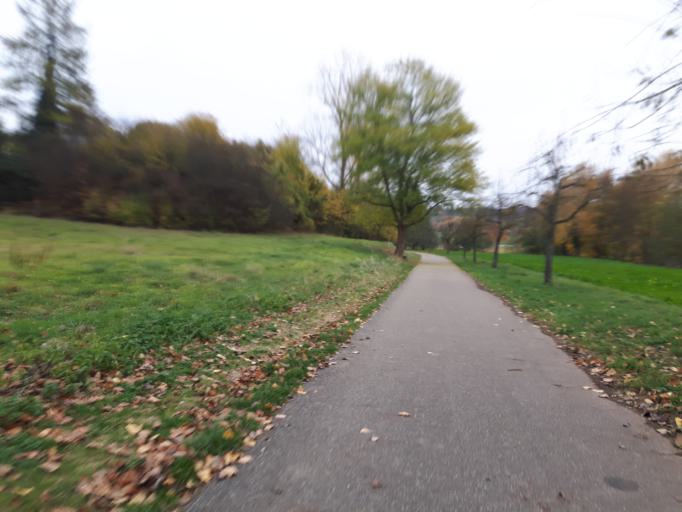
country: DE
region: Baden-Wuerttemberg
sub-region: Karlsruhe Region
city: Ostringen
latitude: 49.1742
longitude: 8.7595
